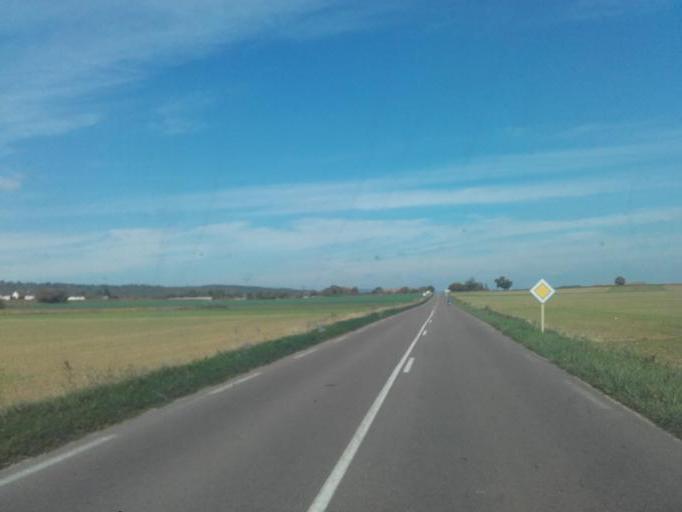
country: FR
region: Bourgogne
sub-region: Departement de Saone-et-Loire
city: Rully
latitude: 46.8663
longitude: 4.7525
